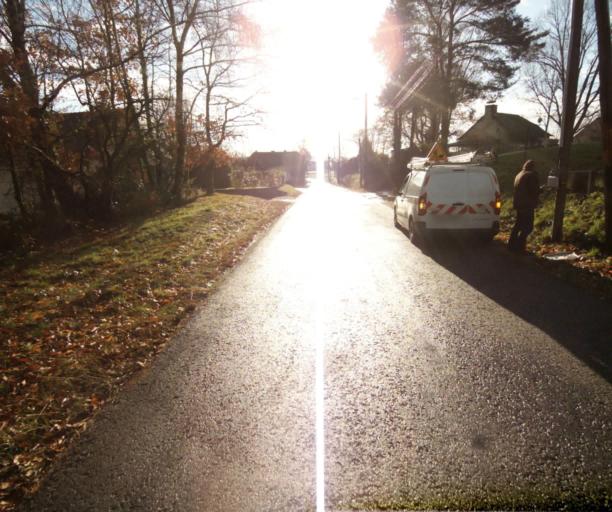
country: FR
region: Limousin
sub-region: Departement de la Correze
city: Saint-Mexant
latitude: 45.2429
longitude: 1.6311
